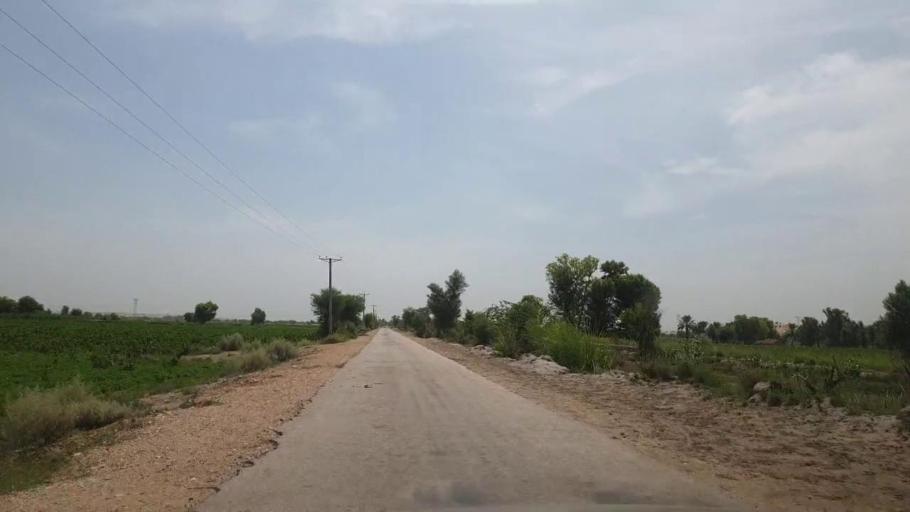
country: PK
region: Sindh
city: Kot Diji
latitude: 27.1096
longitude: 69.0238
